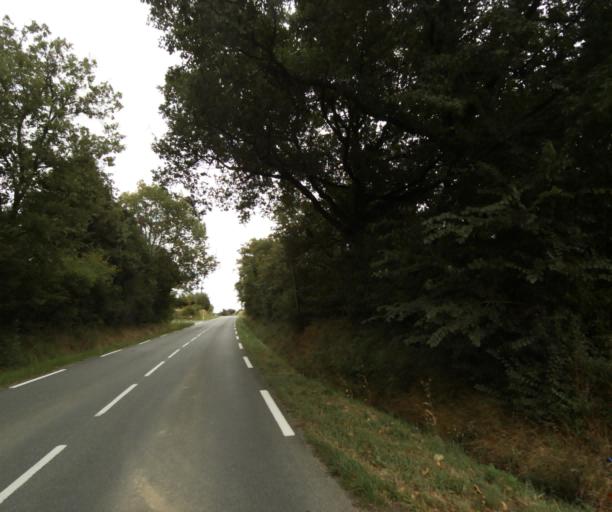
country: FR
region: Midi-Pyrenees
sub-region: Departement de la Haute-Garonne
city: Balma
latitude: 43.5994
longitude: 1.5224
